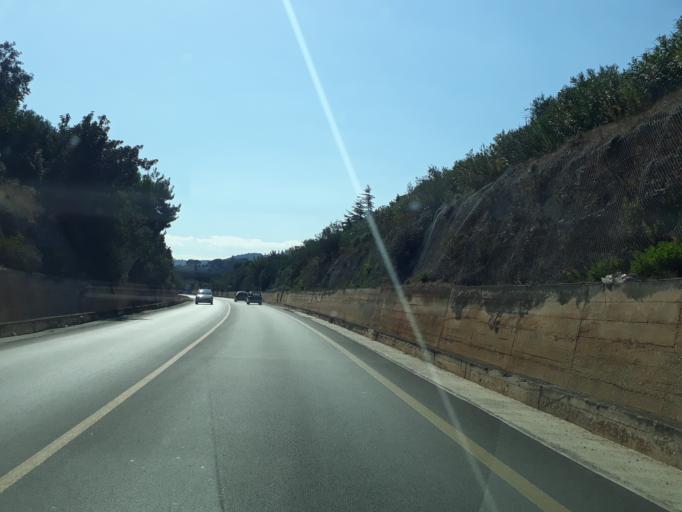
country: IT
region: Apulia
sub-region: Provincia di Brindisi
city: Fasano
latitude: 40.8367
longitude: 17.3505
